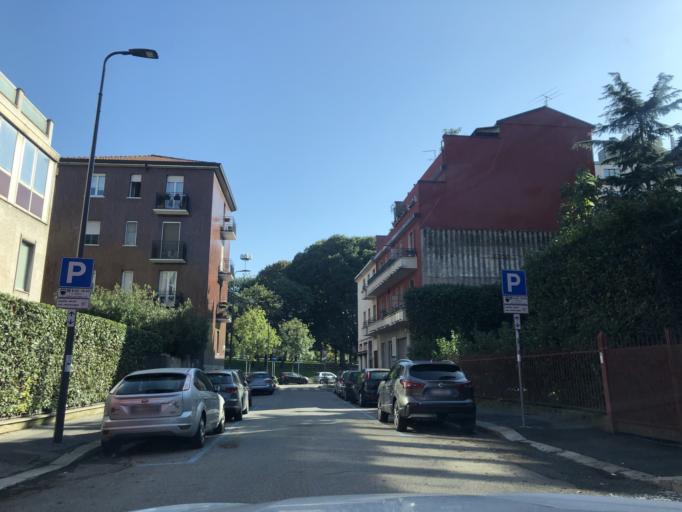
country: IT
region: Lombardy
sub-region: Citta metropolitana di Milano
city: Milano
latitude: 45.4941
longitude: 9.1979
